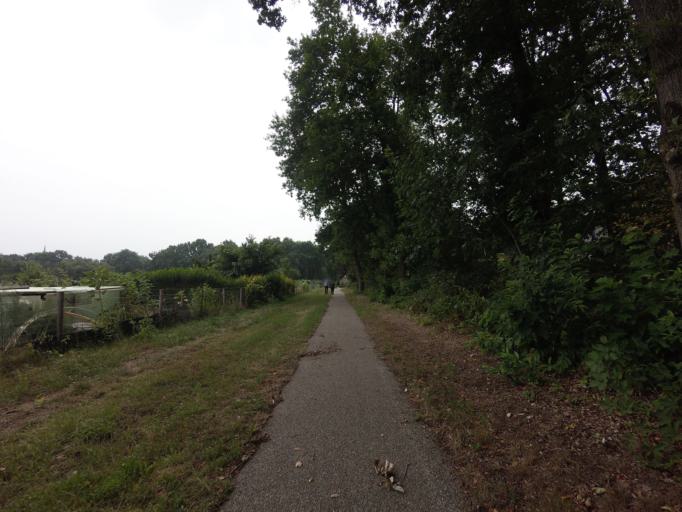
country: NL
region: Utrecht
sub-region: Gemeente Rhenen
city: Rhenen
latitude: 51.9695
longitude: 5.5625
